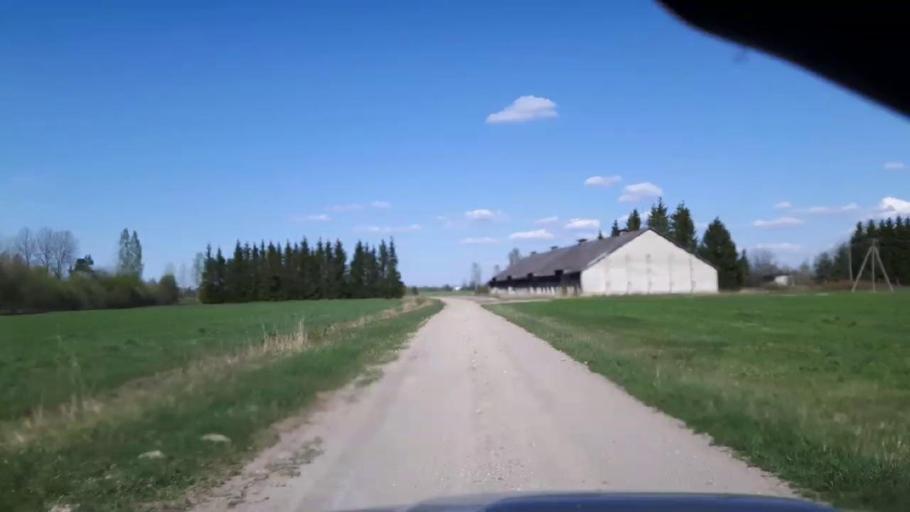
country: EE
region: Paernumaa
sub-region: Tootsi vald
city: Tootsi
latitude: 58.5244
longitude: 24.8212
